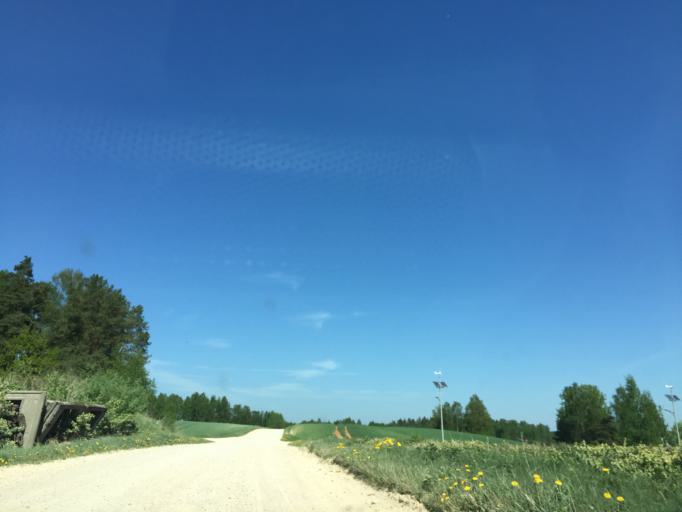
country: LV
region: Ikskile
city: Ikskile
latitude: 56.8655
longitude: 24.5021
